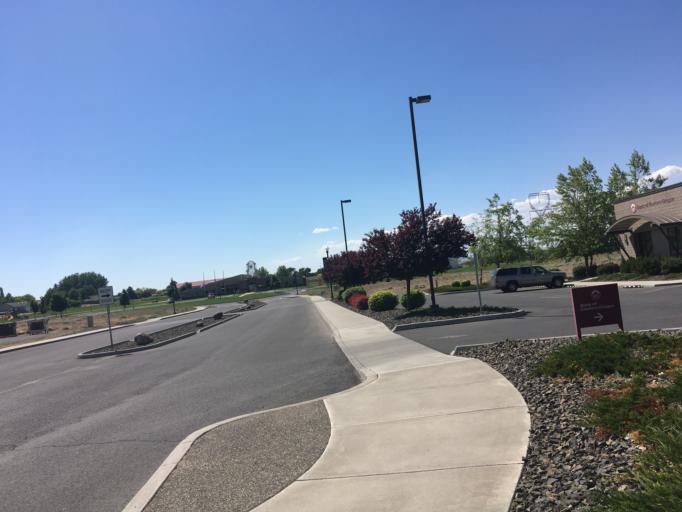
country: US
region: Oregon
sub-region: Morrow County
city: Boardman
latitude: 45.8328
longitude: -119.7006
